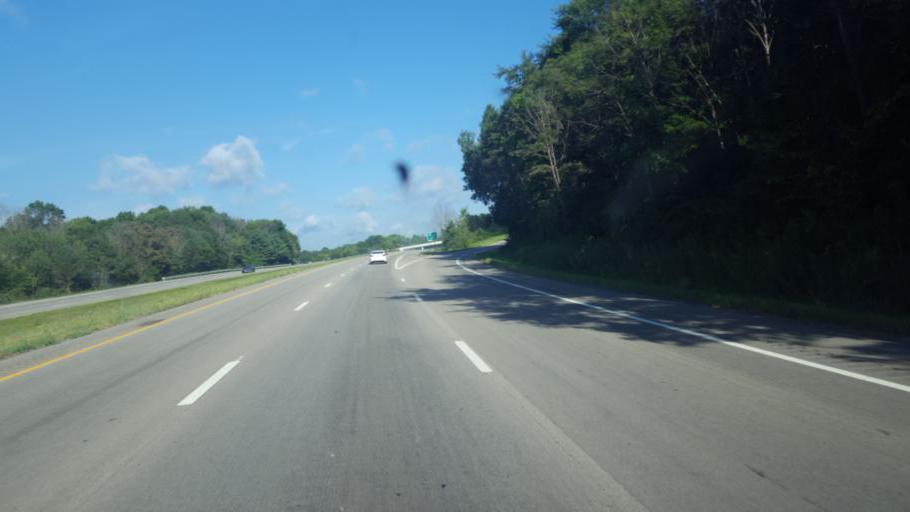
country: US
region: Ohio
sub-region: Stark County
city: Brewster
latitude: 40.7659
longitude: -81.5769
